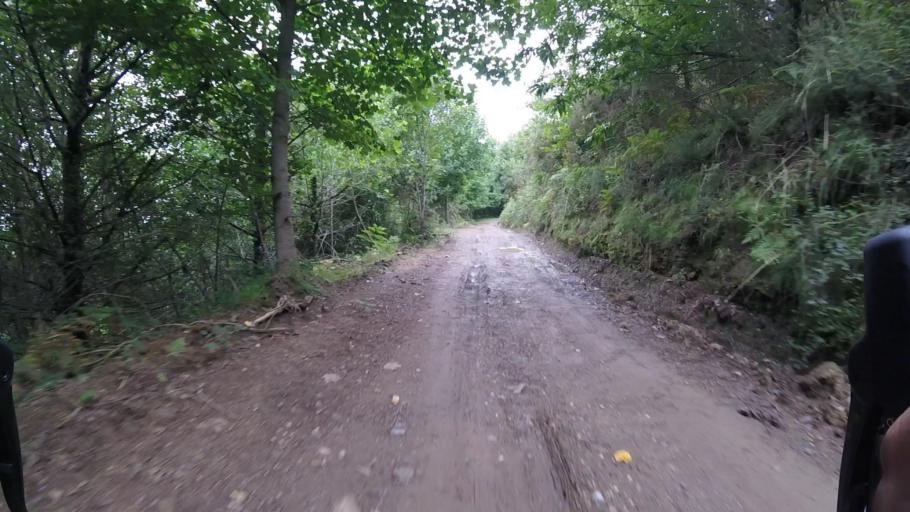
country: ES
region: Basque Country
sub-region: Provincia de Guipuzcoa
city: Errenteria
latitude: 43.2627
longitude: -1.8520
